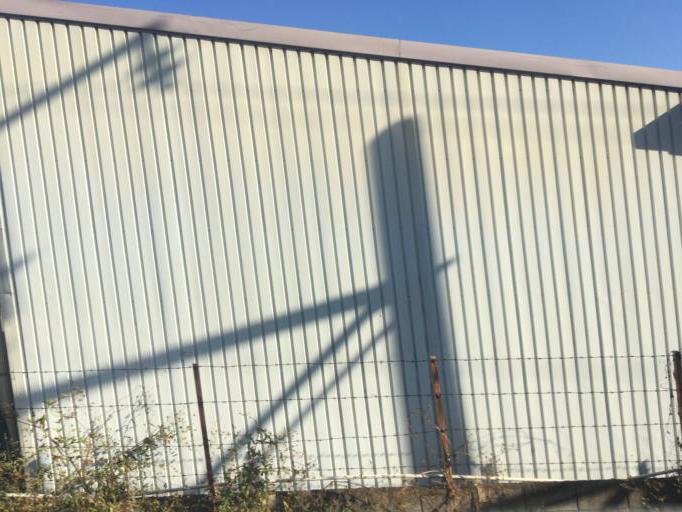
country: JP
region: Gunma
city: Maebashi-shi
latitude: 36.3725
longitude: 139.1063
